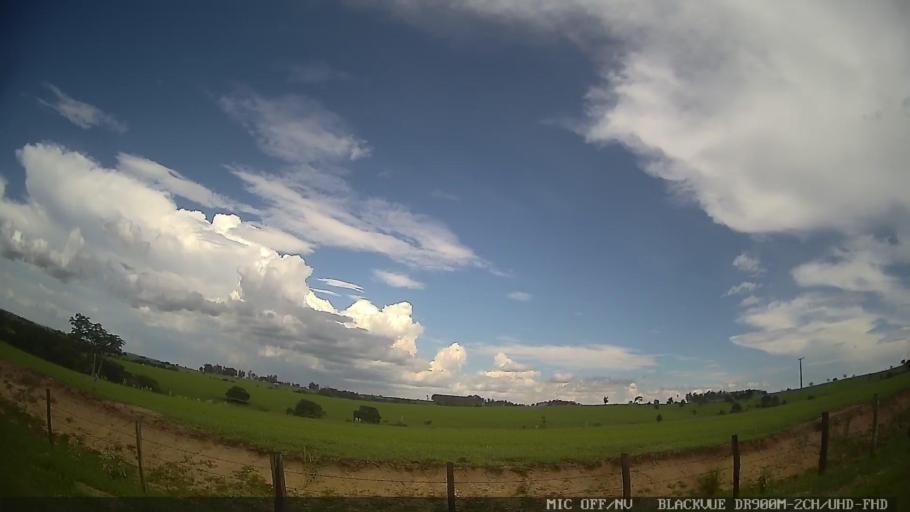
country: BR
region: Sao Paulo
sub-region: Conchas
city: Conchas
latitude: -22.9678
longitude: -47.9841
